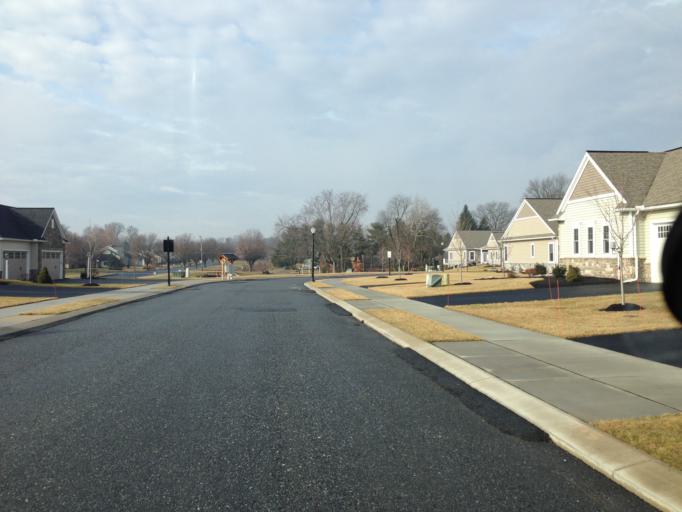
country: US
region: Pennsylvania
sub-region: Lancaster County
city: Lititz
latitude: 40.1485
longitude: -76.2932
